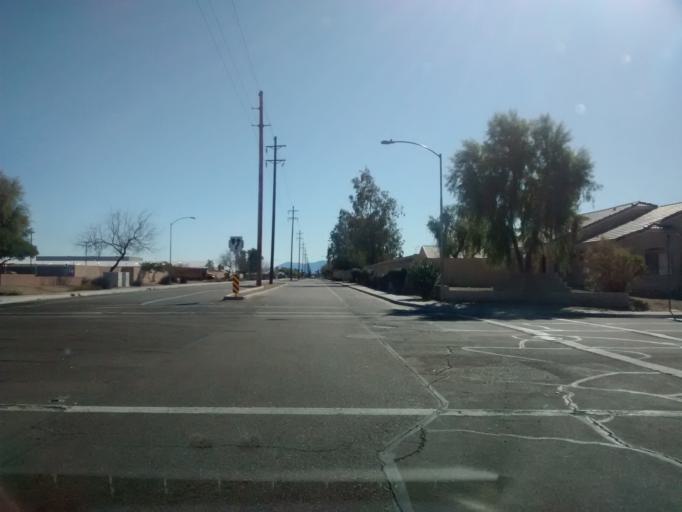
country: US
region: Arizona
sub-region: Maricopa County
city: Glendale
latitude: 33.5310
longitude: -112.2119
